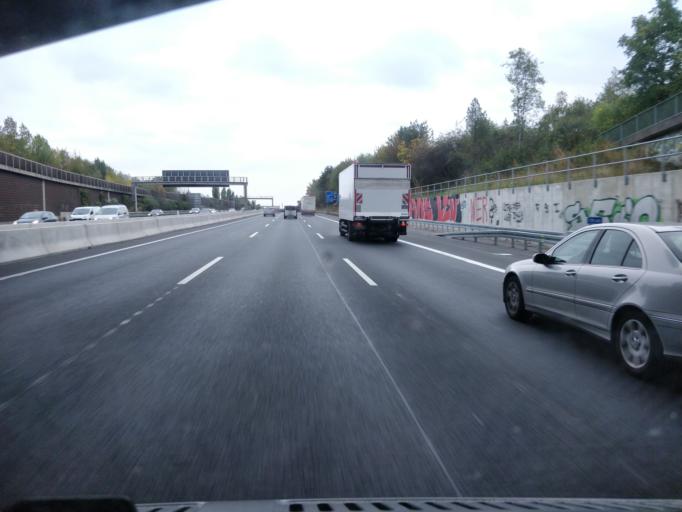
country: DE
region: North Rhine-Westphalia
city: Leichlingen
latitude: 51.1047
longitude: 6.9879
